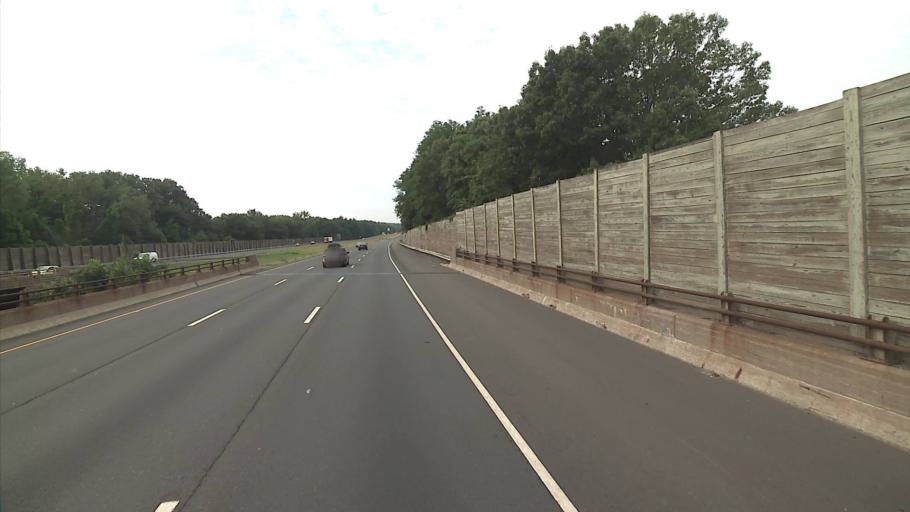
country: US
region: Connecticut
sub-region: Hartford County
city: Plainville
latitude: 41.6608
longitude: -72.8492
